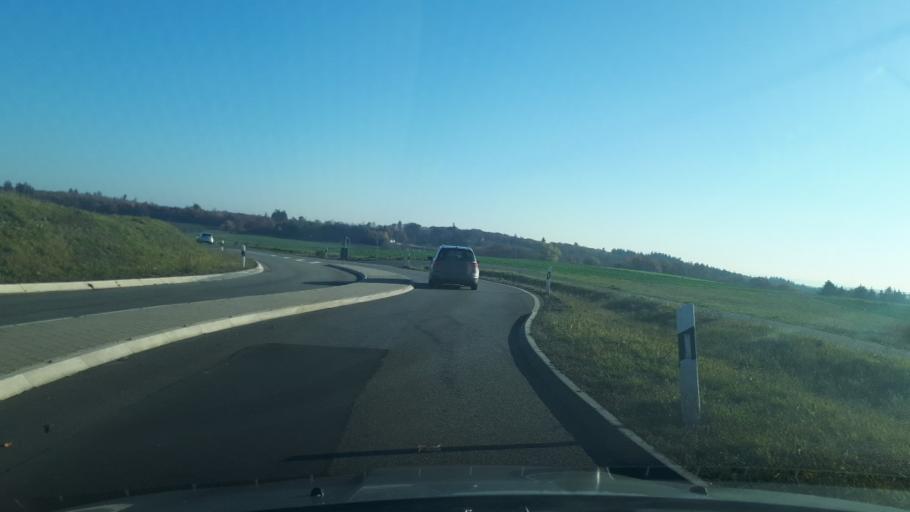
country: DE
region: Rheinland-Pfalz
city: Buchel
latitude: 50.1705
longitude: 7.0870
